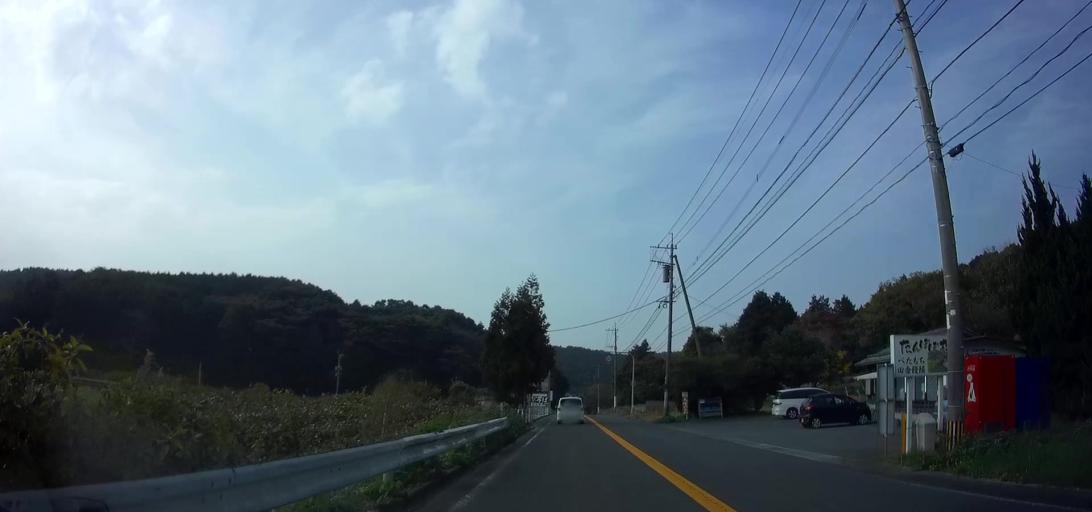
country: JP
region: Nagasaki
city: Shimabara
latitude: 32.7637
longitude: 130.2122
